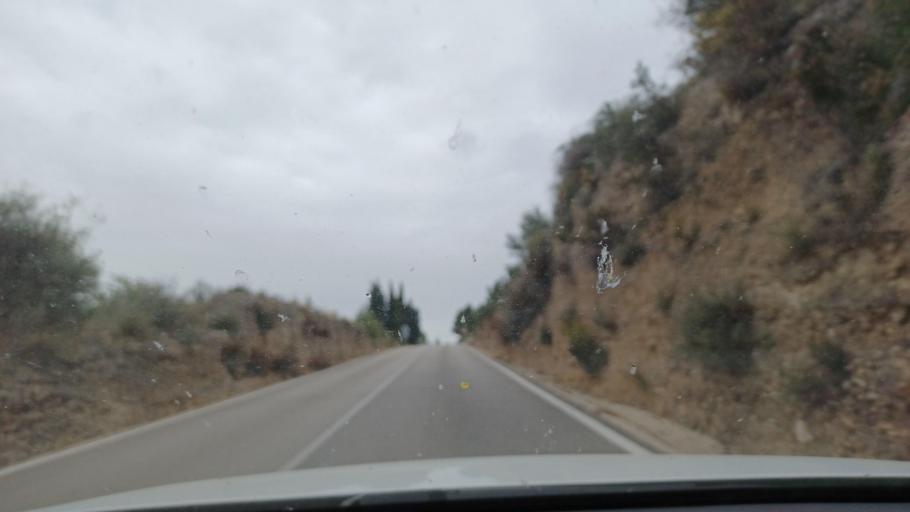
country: ES
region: Valencia
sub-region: Provincia de Castello
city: Rosell
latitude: 40.6320
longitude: 0.2744
